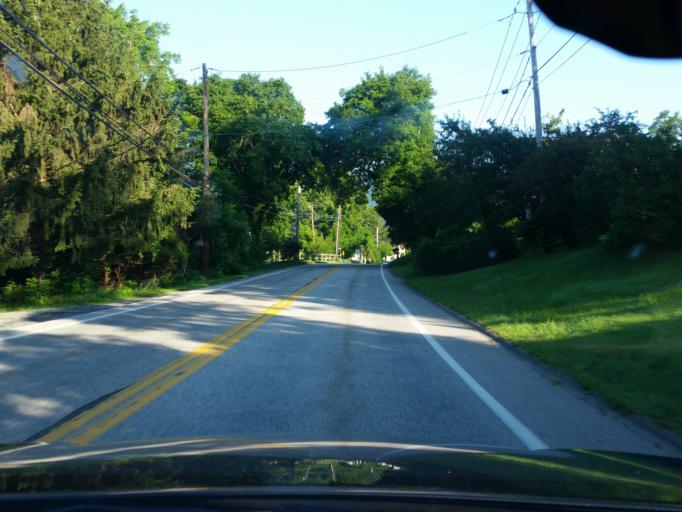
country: US
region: Pennsylvania
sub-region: Perry County
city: Marysville
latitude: 40.3847
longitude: -76.9373
